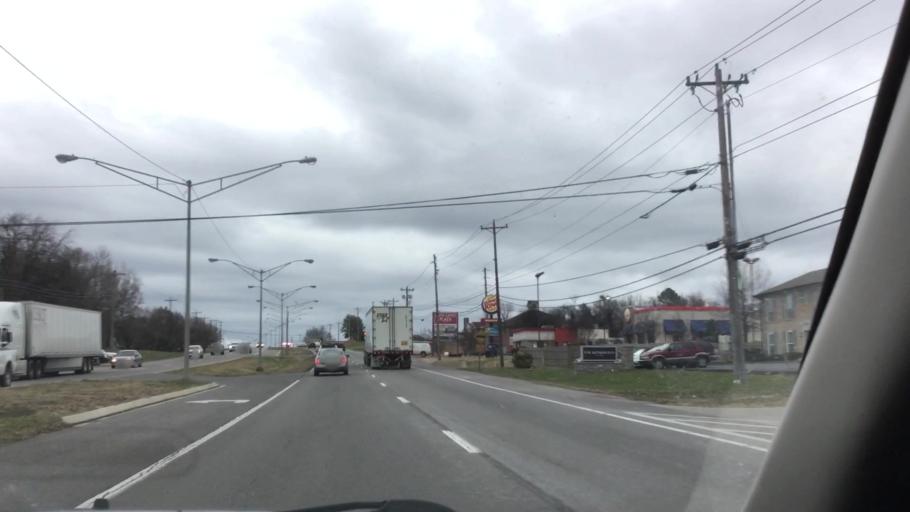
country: US
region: Tennessee
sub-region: Maury County
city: Columbia
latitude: 35.6383
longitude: -87.0159
